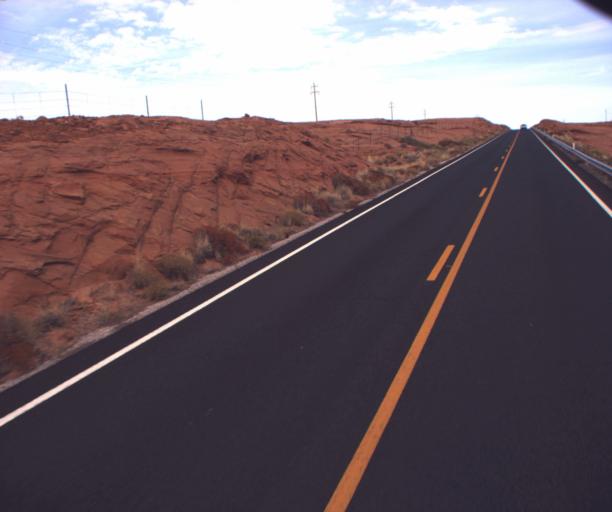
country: US
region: Arizona
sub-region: Apache County
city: Many Farms
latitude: 36.7852
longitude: -109.6550
